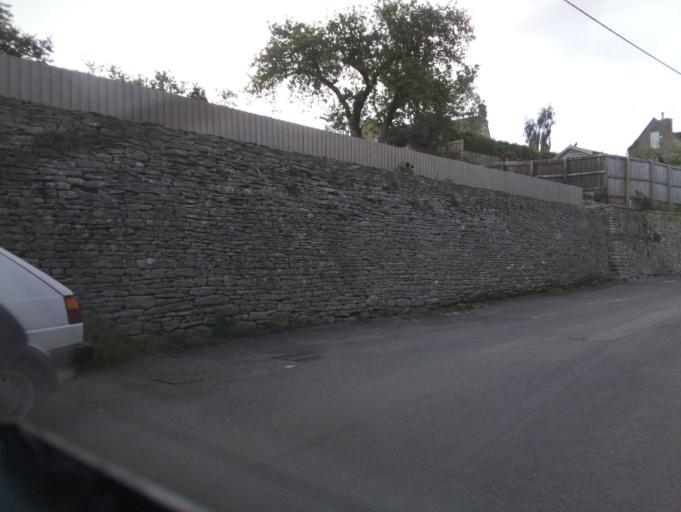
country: GB
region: England
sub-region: Wiltshire
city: Luckington
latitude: 51.5701
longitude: -2.2108
